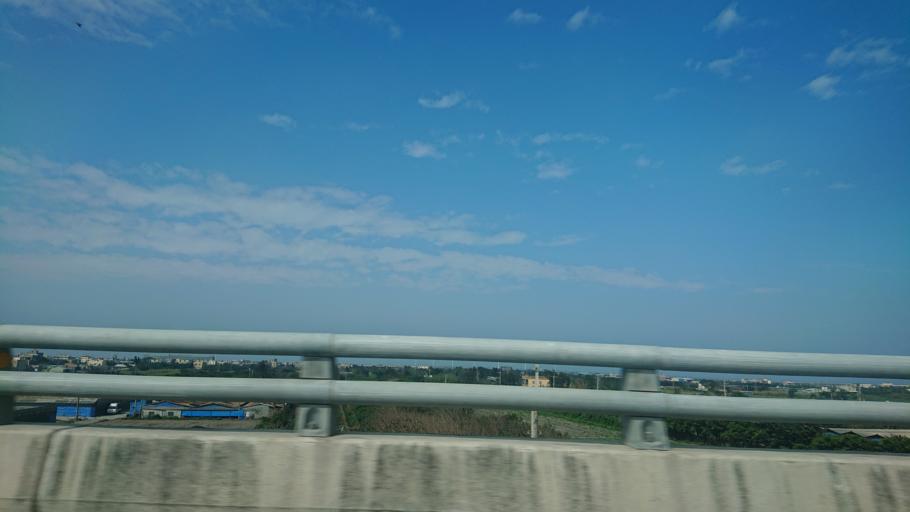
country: TW
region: Taiwan
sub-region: Changhua
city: Chang-hua
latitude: 23.9752
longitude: 120.3612
